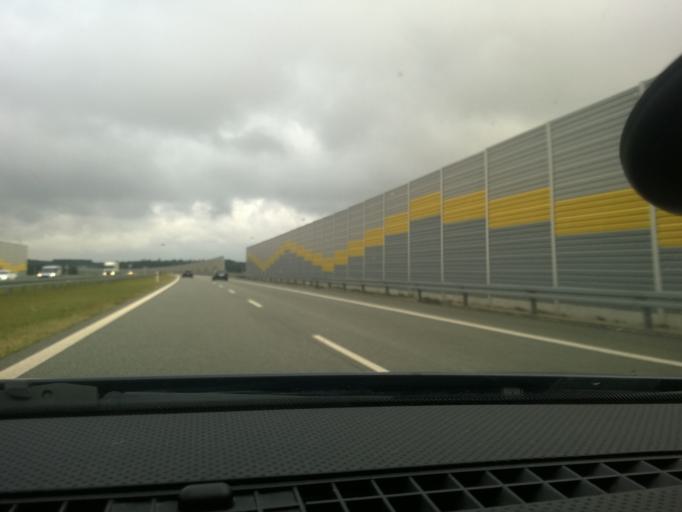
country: PL
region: Lodz Voivodeship
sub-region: Powiat zdunskowolski
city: Zdunska Wola
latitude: 51.5785
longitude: 18.9151
